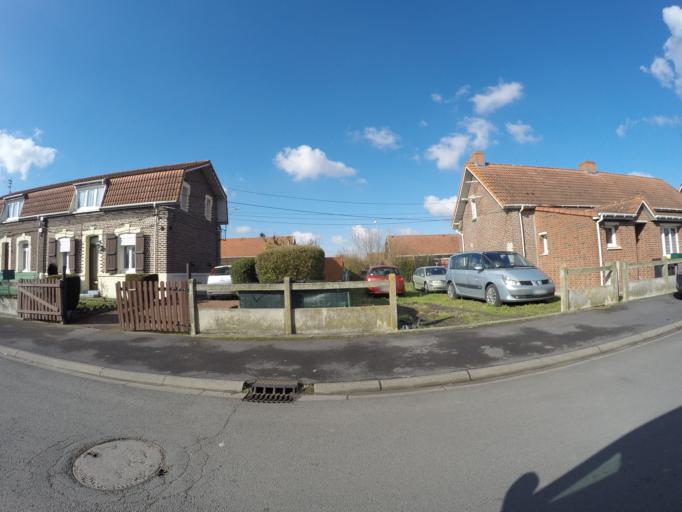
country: FR
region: Nord-Pas-de-Calais
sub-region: Departement du Pas-de-Calais
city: Bully-les-Mines
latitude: 50.4556
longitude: 2.7241
